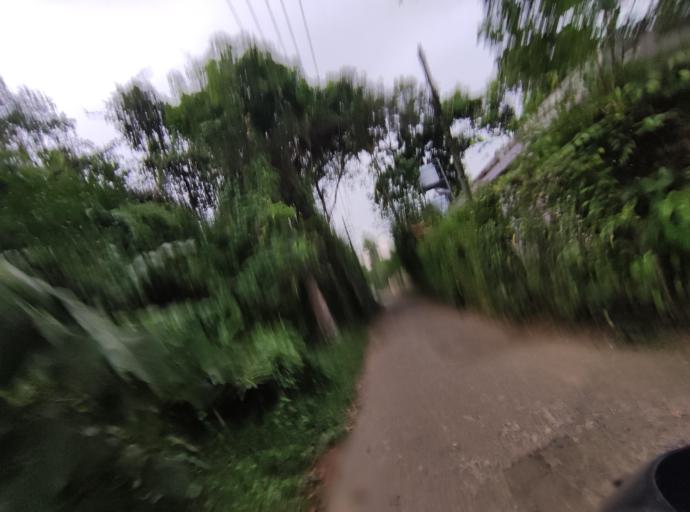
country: IN
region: Kerala
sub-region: Alappuzha
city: Shertallai
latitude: 9.6292
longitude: 76.4284
